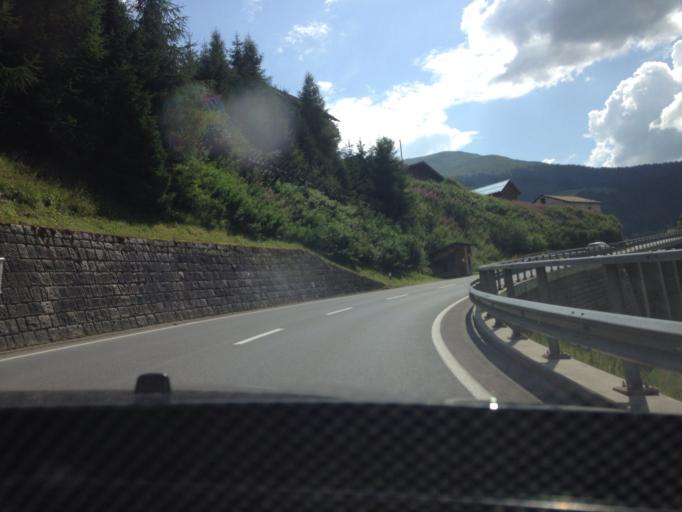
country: CH
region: Grisons
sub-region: Surselva District
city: Disentis
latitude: 46.6751
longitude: 8.8587
